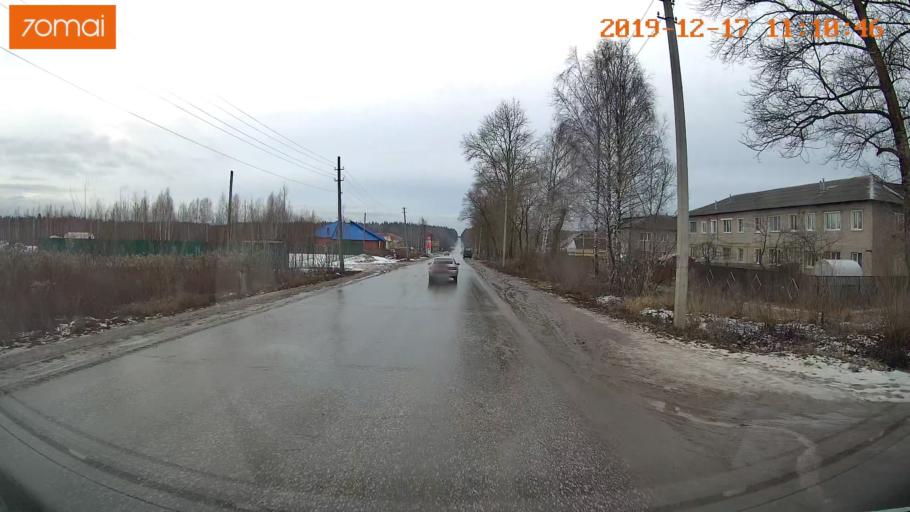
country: RU
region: Vladimir
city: Gus'-Khrustal'nyy
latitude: 55.5906
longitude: 40.6398
